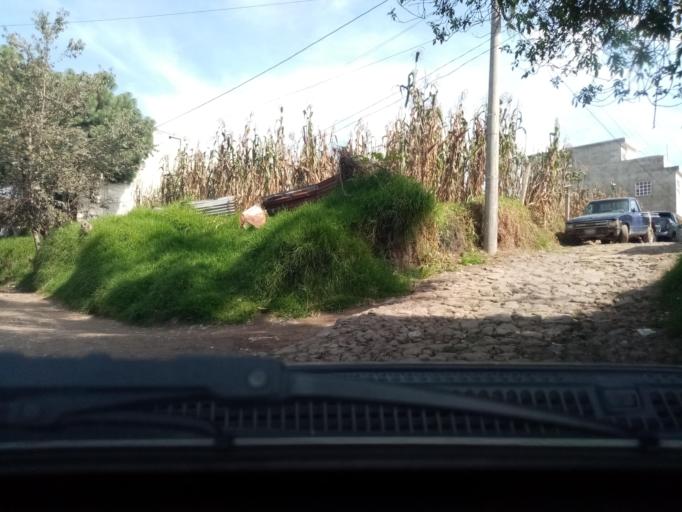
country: GT
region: Quetzaltenango
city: Olintepeque
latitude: 14.8599
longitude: -91.5325
